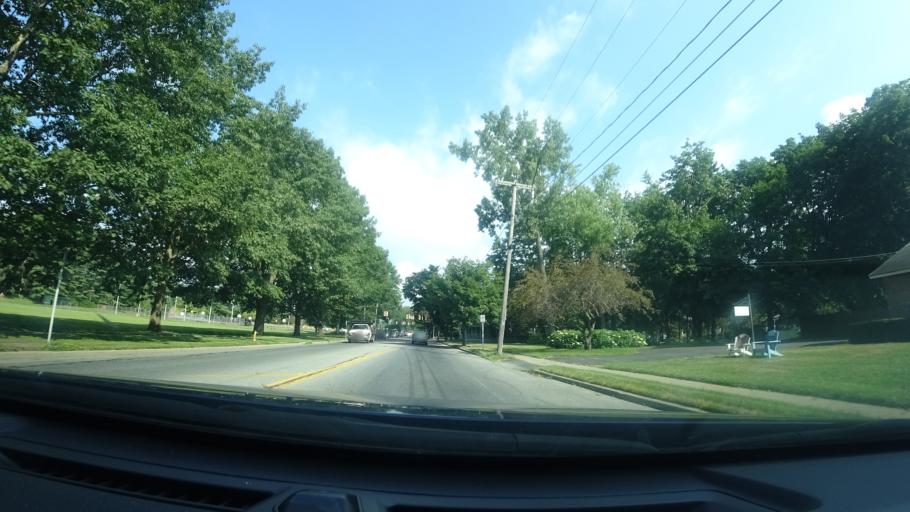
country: US
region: New York
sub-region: Warren County
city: Glens Falls
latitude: 43.3215
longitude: -73.6599
